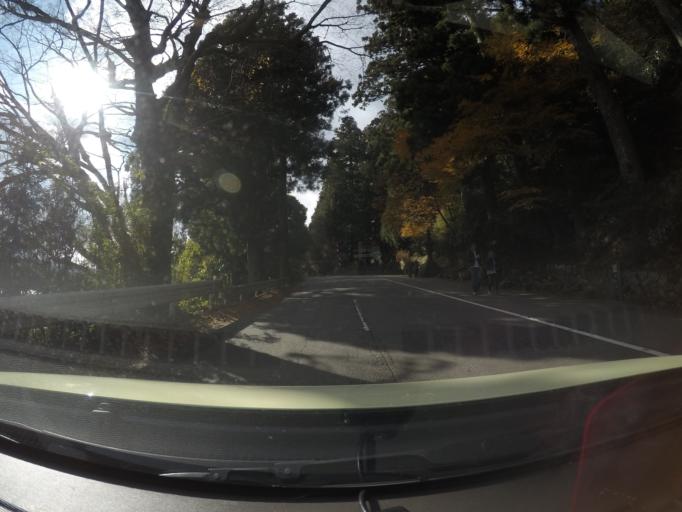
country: JP
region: Kanagawa
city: Hakone
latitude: 35.2042
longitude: 139.0280
